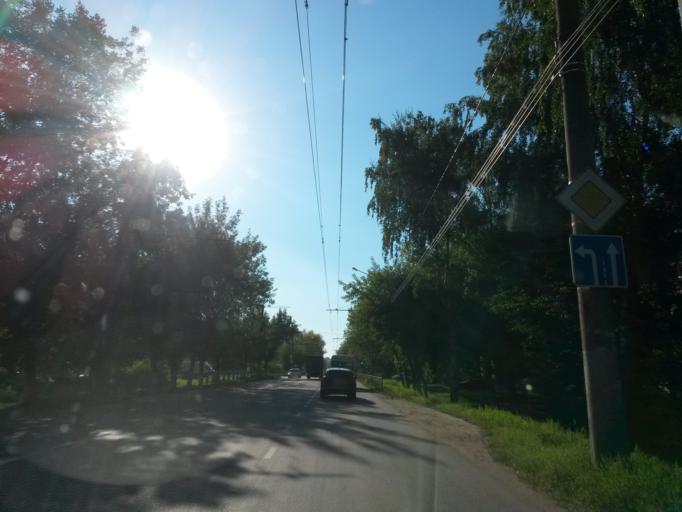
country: RU
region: Ivanovo
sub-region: Gorod Ivanovo
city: Ivanovo
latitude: 56.9981
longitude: 40.9523
